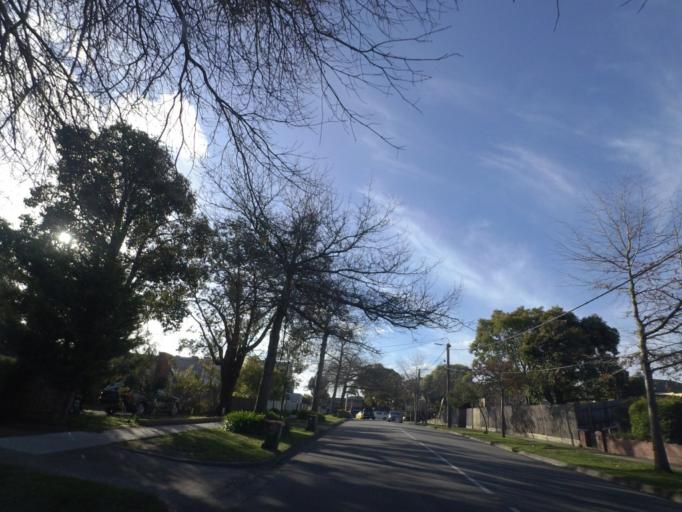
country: AU
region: Victoria
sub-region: Whitehorse
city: Blackburn
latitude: -37.8199
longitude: 145.1409
